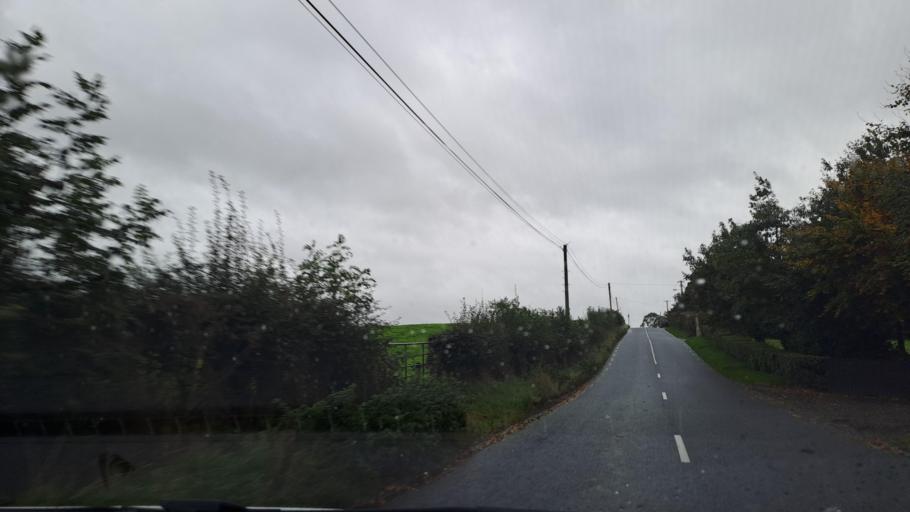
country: IE
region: Leinster
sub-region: Lu
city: Dundalk
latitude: 53.9825
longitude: -6.4949
